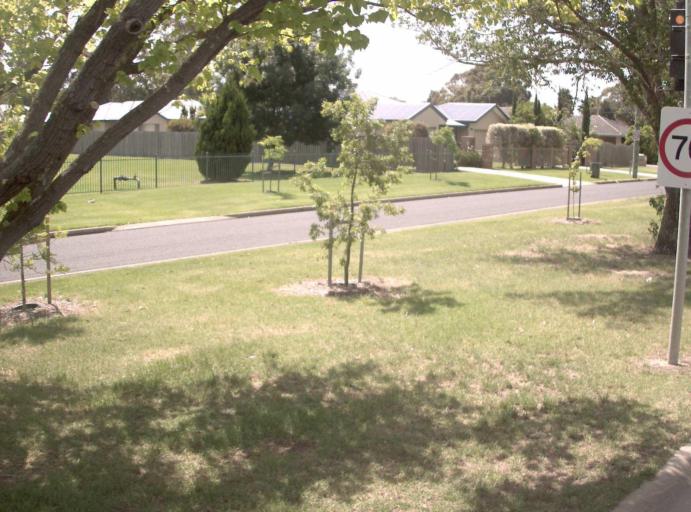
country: AU
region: Victoria
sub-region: Wellington
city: Sale
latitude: -38.0946
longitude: 147.0686
